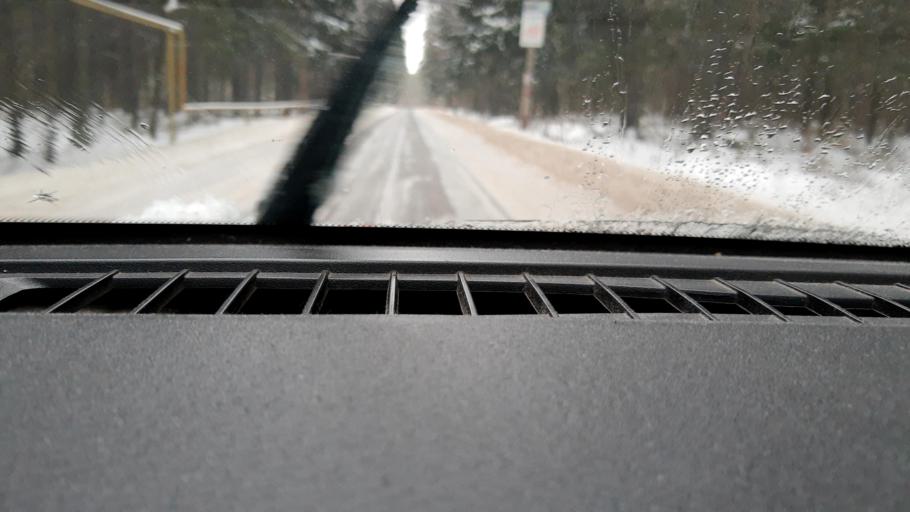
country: RU
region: Nizjnij Novgorod
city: Afonino
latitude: 56.1770
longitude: 44.0767
